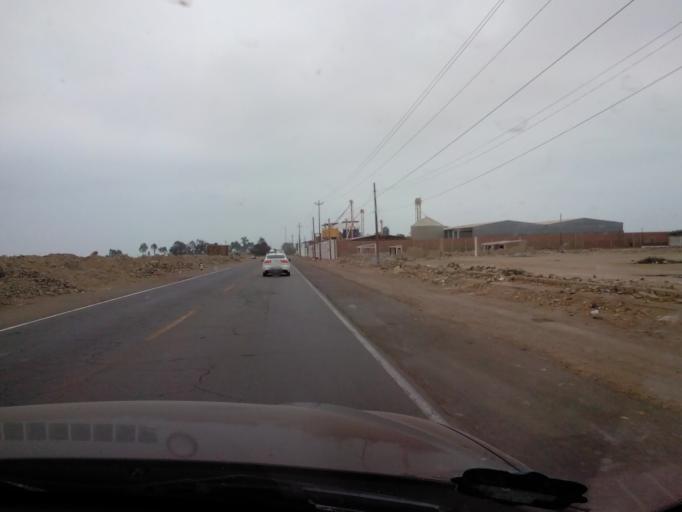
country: PE
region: Ica
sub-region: Provincia de Chincha
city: Sunampe
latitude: -13.4109
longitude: -76.1742
